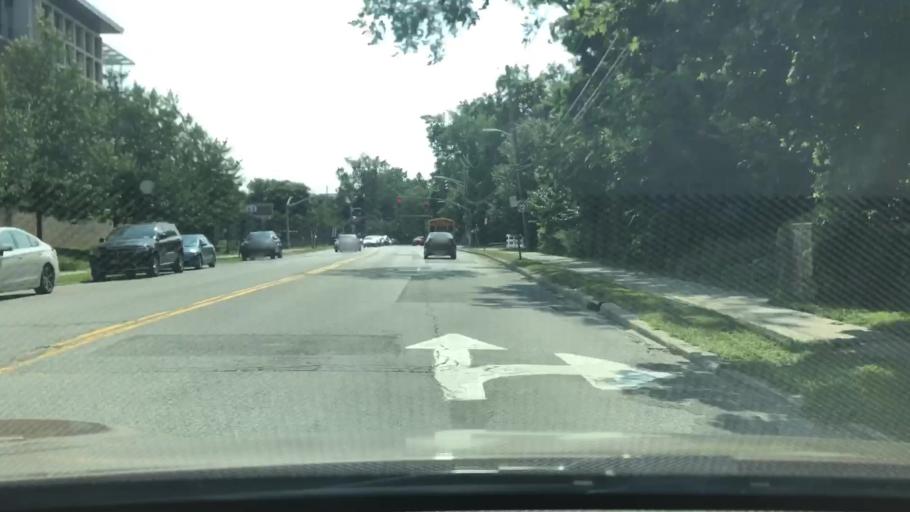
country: US
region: New York
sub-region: Westchester County
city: Pelham
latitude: 40.9043
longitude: -73.8129
